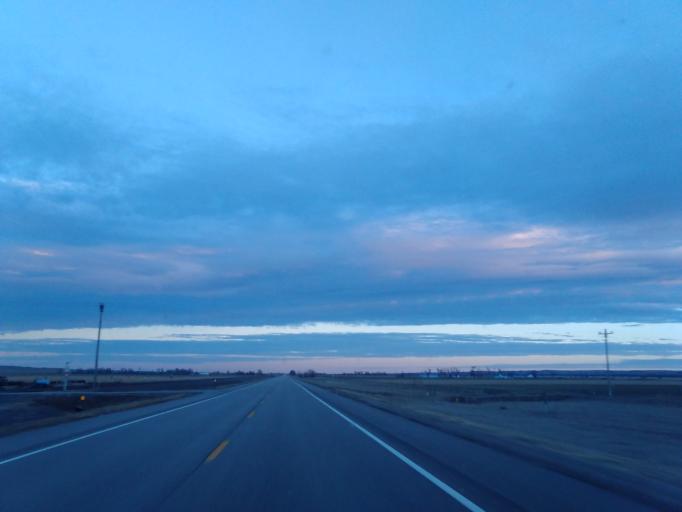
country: US
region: Nebraska
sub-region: Garden County
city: Oshkosh
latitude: 41.4008
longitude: -102.3292
